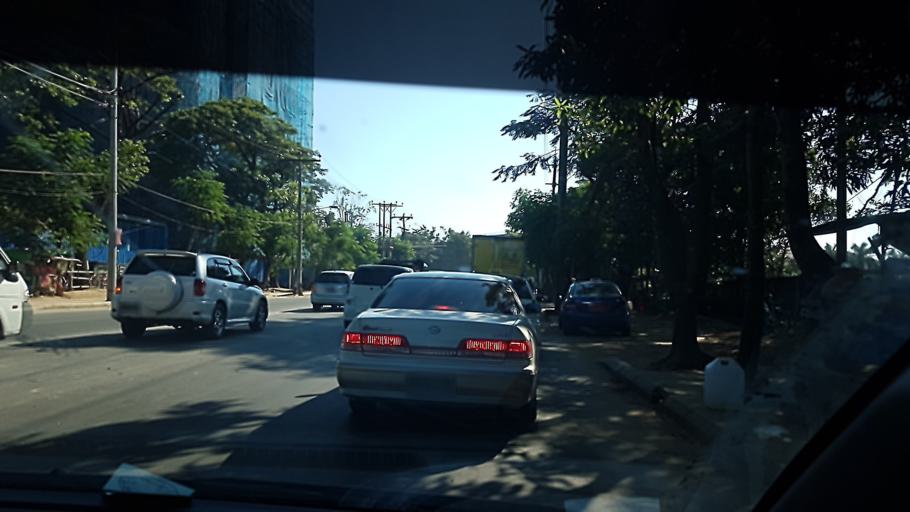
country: MM
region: Yangon
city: Yangon
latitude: 16.8576
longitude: 96.1285
